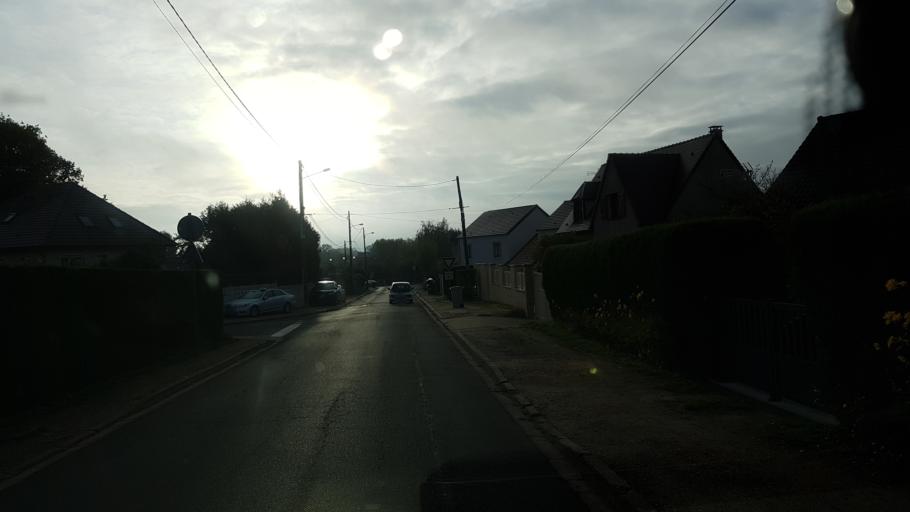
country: FR
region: Ile-de-France
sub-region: Departement de l'Essonne
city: Les Molieres
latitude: 48.6720
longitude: 2.0613
